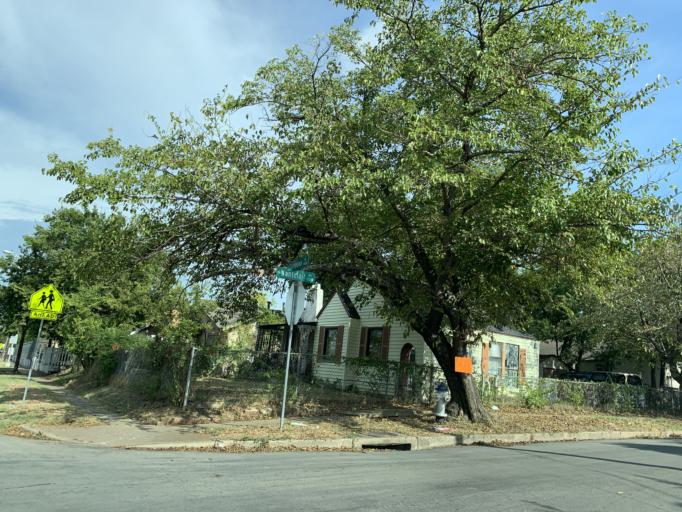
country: US
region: Texas
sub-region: Dallas County
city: Cockrell Hill
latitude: 32.7350
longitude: -96.8469
